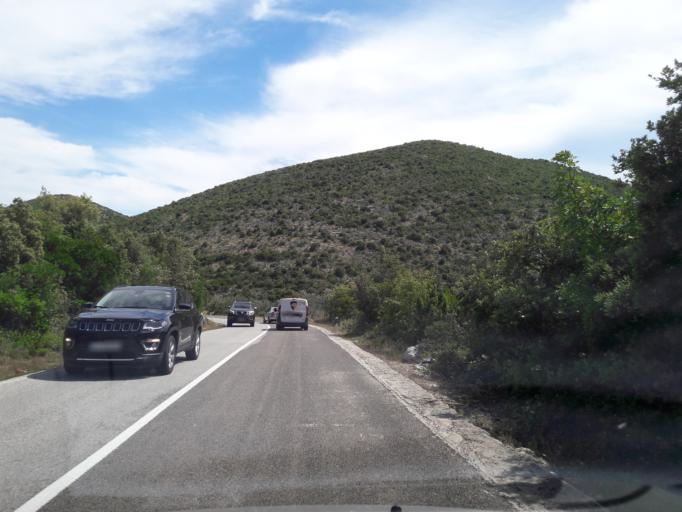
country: HR
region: Dubrovacko-Neretvanska
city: Ston
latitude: 42.8376
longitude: 17.6341
